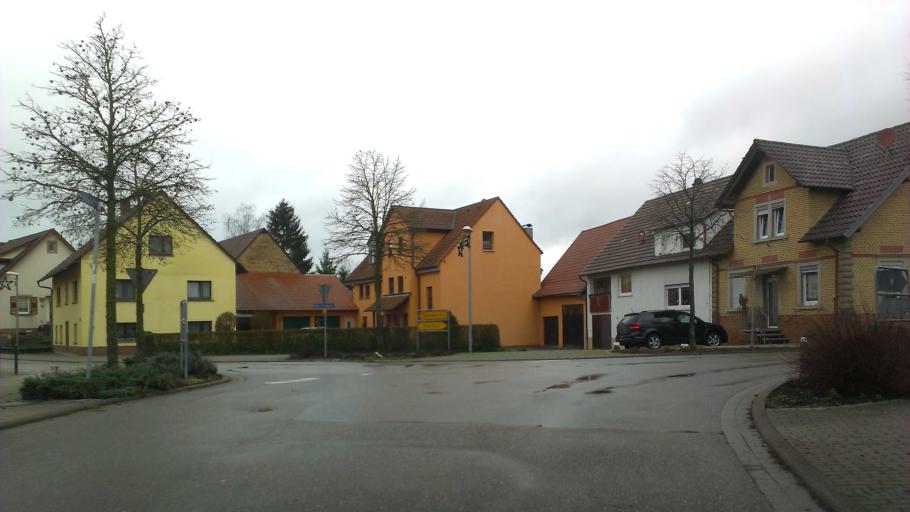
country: DE
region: Baden-Wuerttemberg
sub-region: Karlsruhe Region
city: Oberderdingen
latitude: 49.0871
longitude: 8.7876
